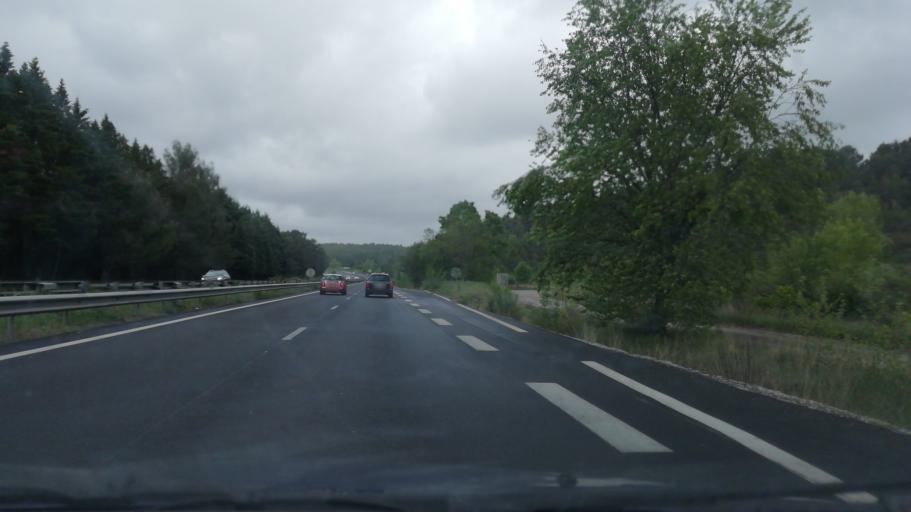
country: FR
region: Languedoc-Roussillon
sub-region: Departement de l'Herault
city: Saint-Clement-de-Riviere
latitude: 43.6654
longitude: 3.8286
